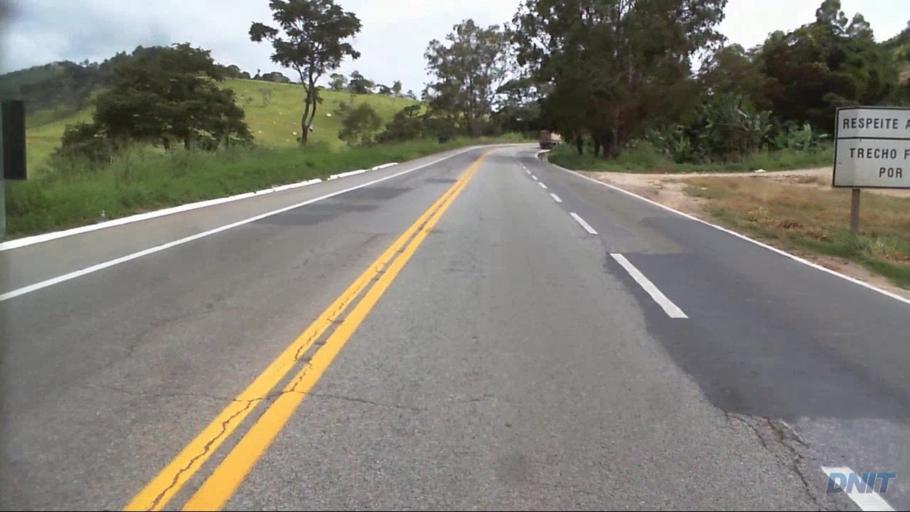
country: BR
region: Minas Gerais
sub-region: Caete
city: Caete
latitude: -19.7230
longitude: -43.5779
